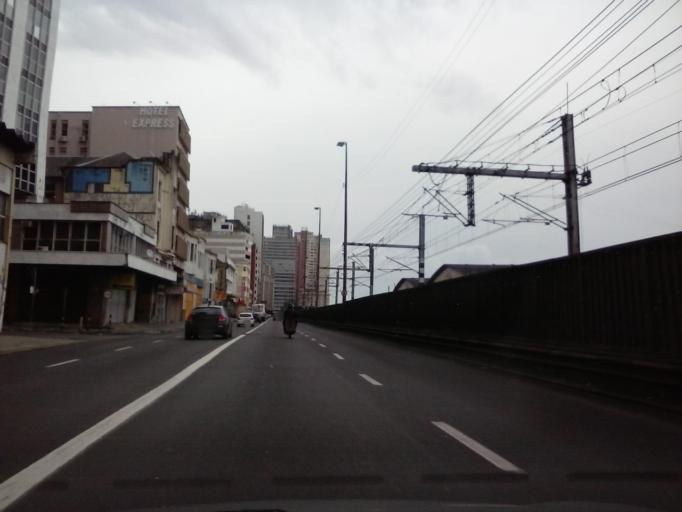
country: BR
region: Rio Grande do Sul
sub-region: Porto Alegre
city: Porto Alegre
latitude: -30.0243
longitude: -51.2233
